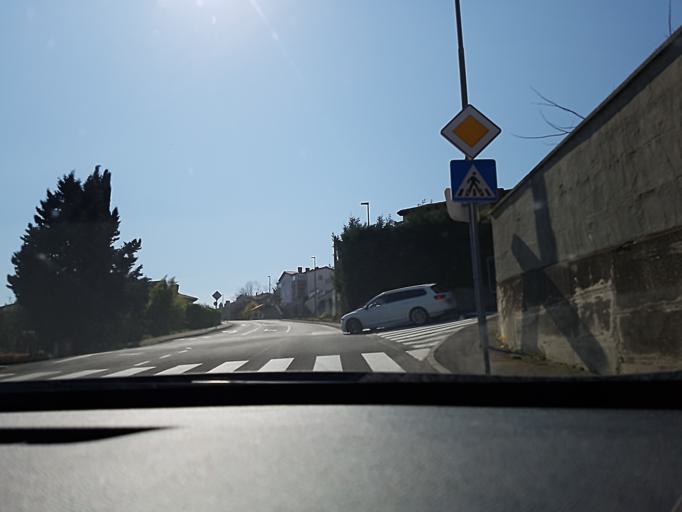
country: SI
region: Koper-Capodistria
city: Koper
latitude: 45.5457
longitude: 13.7031
